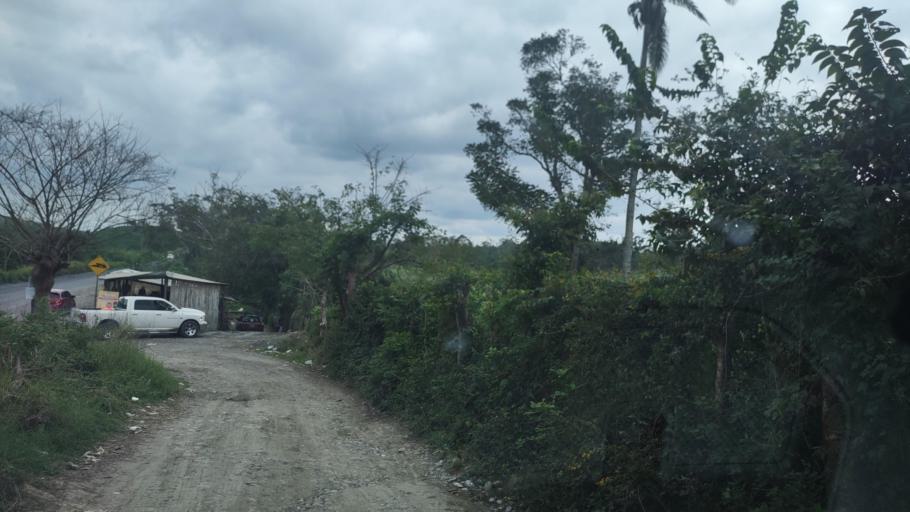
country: MX
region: Veracruz
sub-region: Papantla
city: Polutla
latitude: 20.4650
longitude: -97.2552
